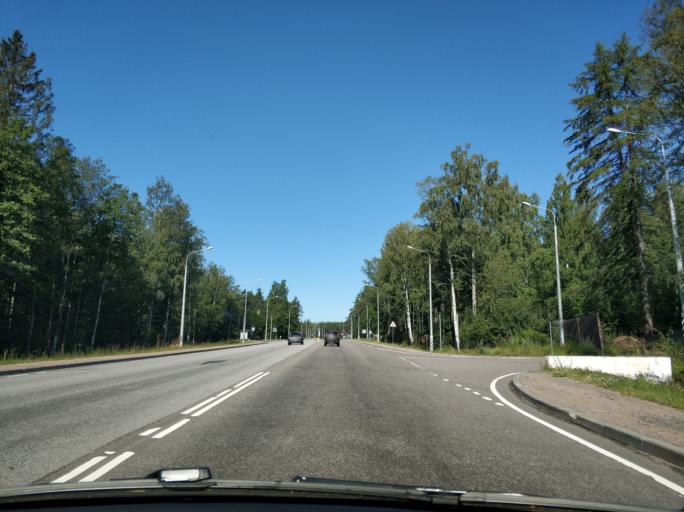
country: RU
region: Leningrad
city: Sapernoye
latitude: 60.6829
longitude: 29.9922
